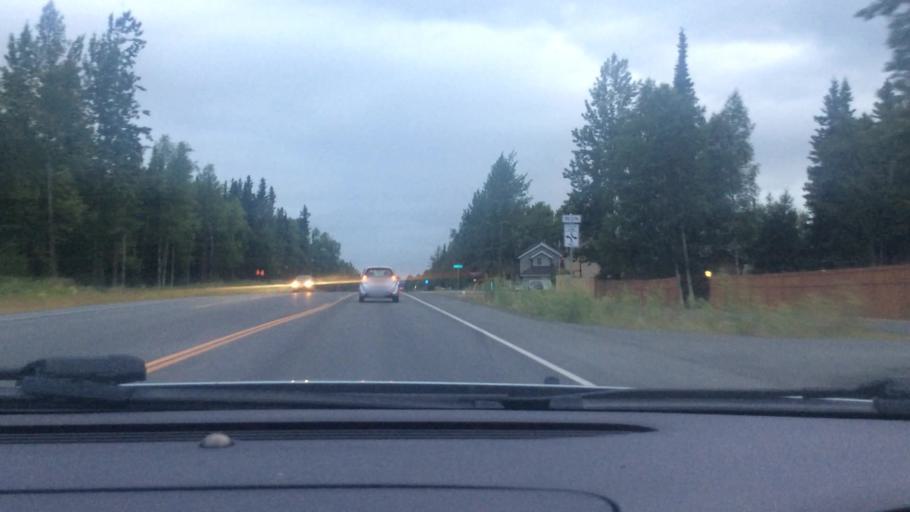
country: US
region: Alaska
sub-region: Anchorage Municipality
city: Anchorage
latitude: 61.1376
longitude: -149.8065
